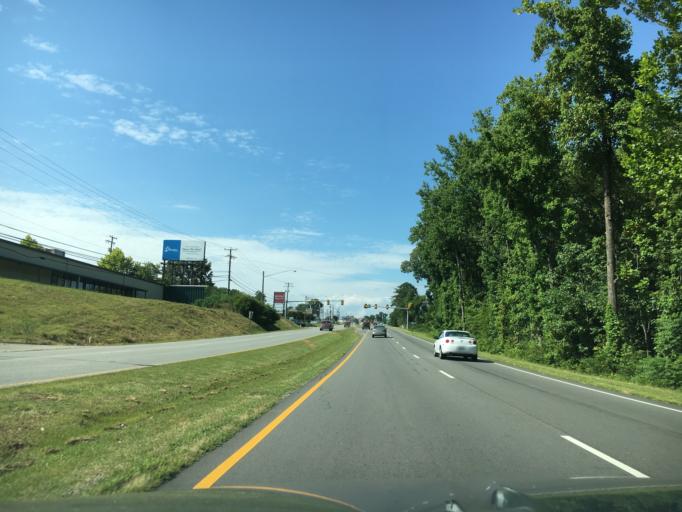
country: US
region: Virginia
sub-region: Halifax County
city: South Boston
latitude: 36.7293
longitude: -78.9186
